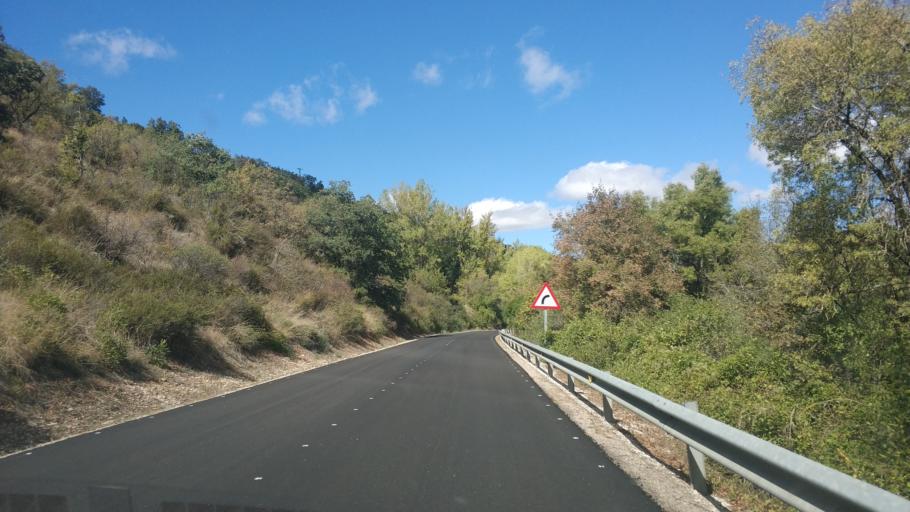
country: ES
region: Castille and Leon
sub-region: Provincia de Burgos
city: Covarrubias
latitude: 42.0529
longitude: -3.5237
